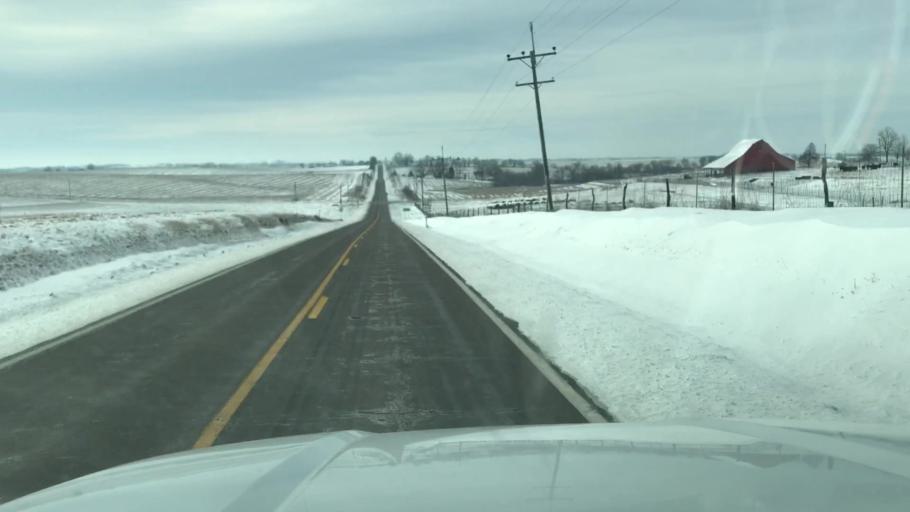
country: US
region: Missouri
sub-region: Holt County
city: Oregon
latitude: 40.0823
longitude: -95.1355
